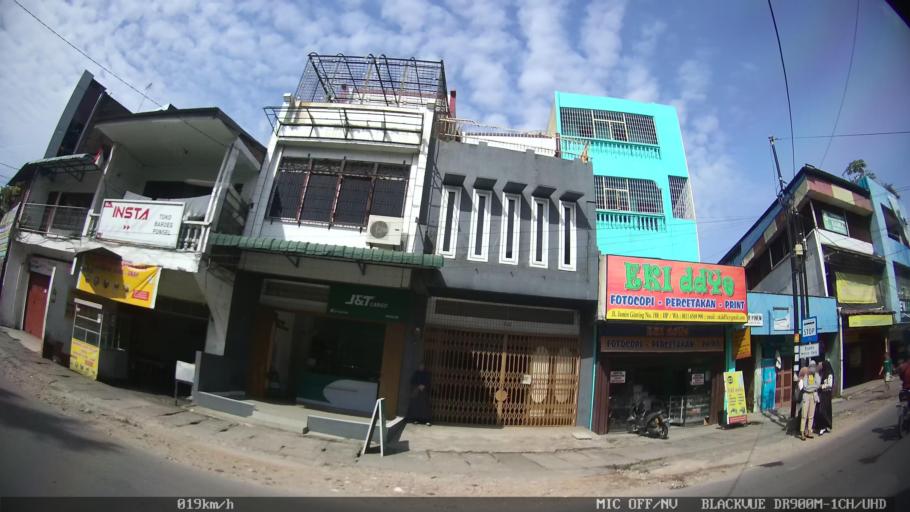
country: ID
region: North Sumatra
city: Medan
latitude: 3.5677
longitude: 98.6606
